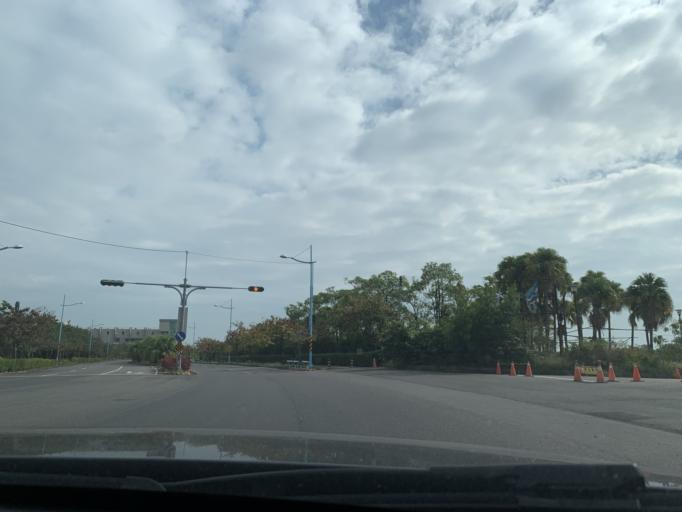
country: TW
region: Taiwan
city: Fengshan
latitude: 22.4544
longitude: 120.4860
